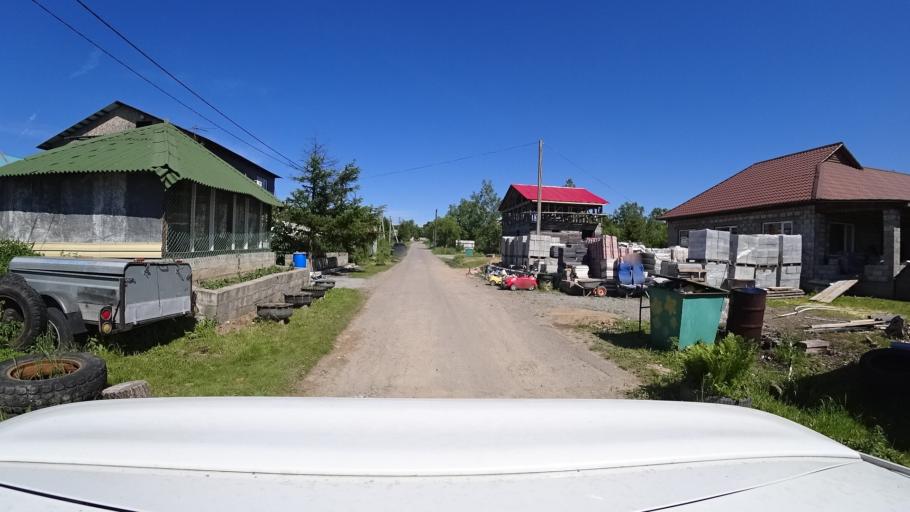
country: RU
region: Khabarovsk Krai
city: Topolevo
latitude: 48.5562
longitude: 135.1865
